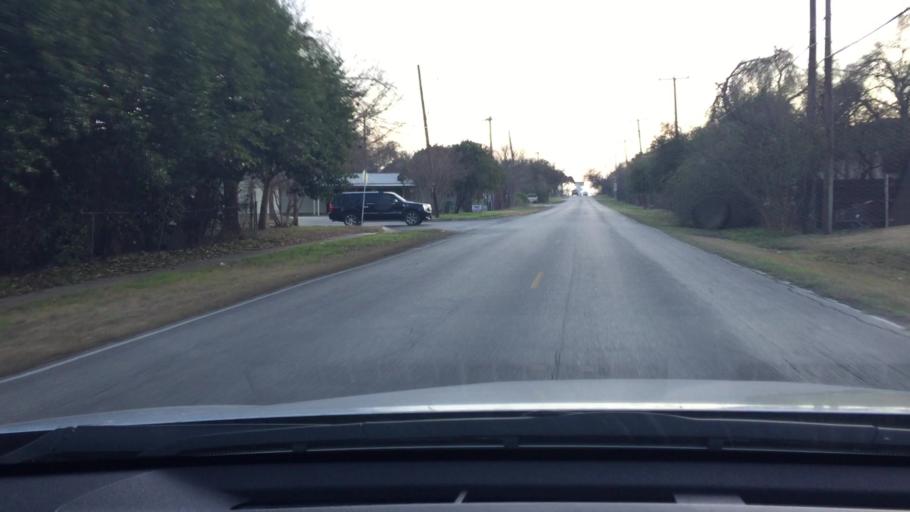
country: US
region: Texas
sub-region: Bexar County
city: Terrell Hills
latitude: 29.4906
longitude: -98.4271
